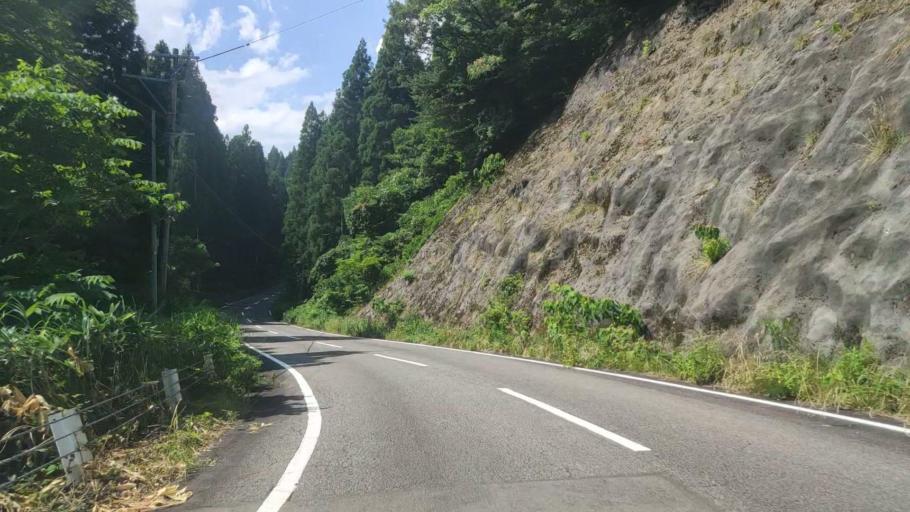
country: JP
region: Fukui
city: Katsuyama
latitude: 36.2333
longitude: 136.5307
